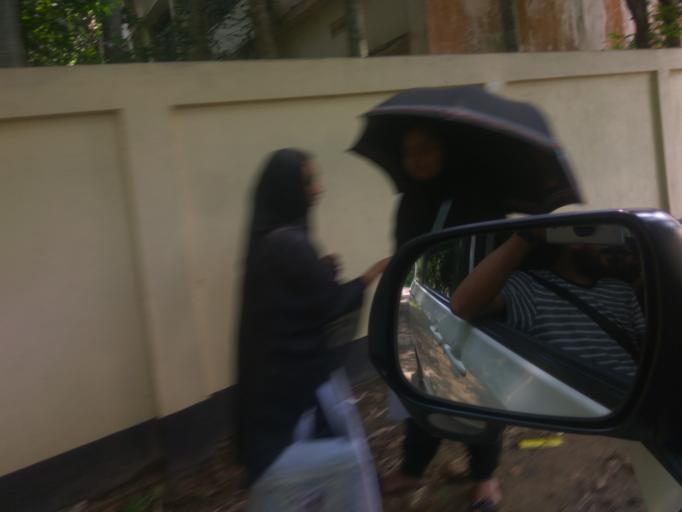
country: IN
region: Assam
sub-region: Karimganj
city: Karimganj
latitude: 24.8116
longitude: 92.1804
